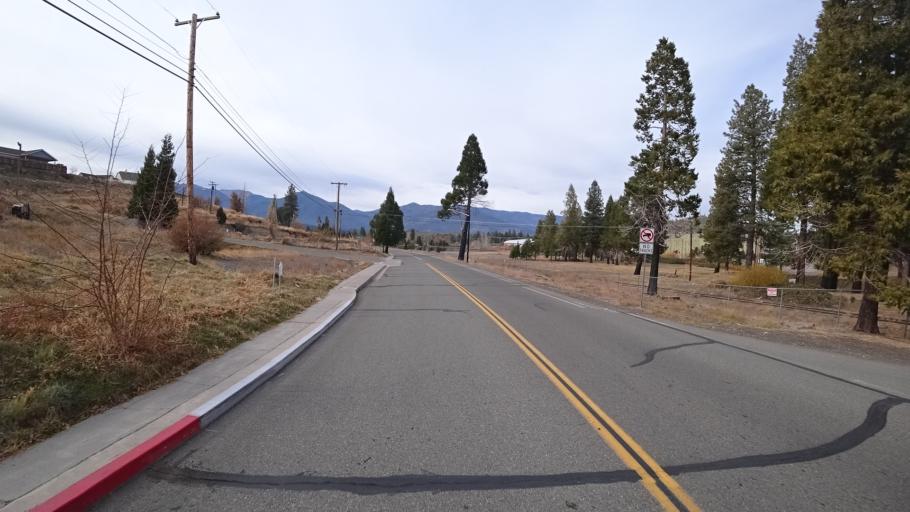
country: US
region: California
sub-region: Siskiyou County
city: Weed
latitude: 41.4313
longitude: -122.3814
